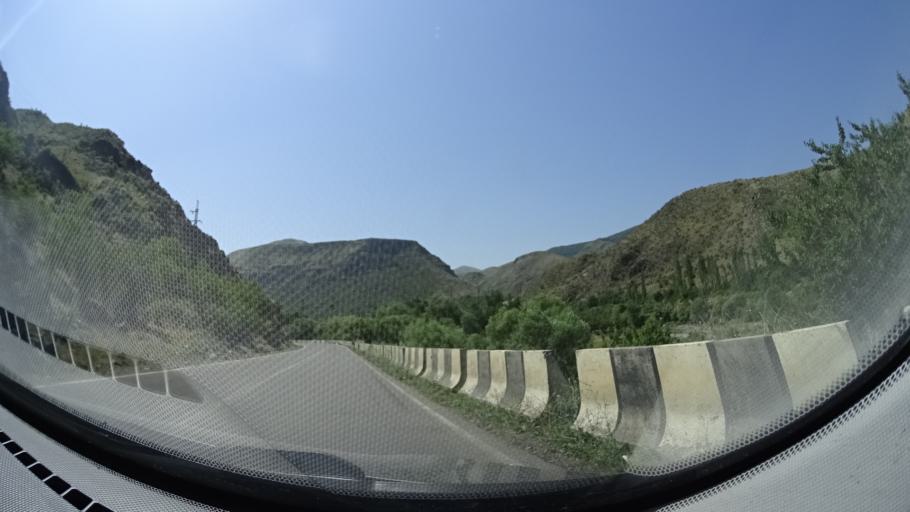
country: GE
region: Samtskhe-Javakheti
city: Aspindza
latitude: 41.4909
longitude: 43.2670
